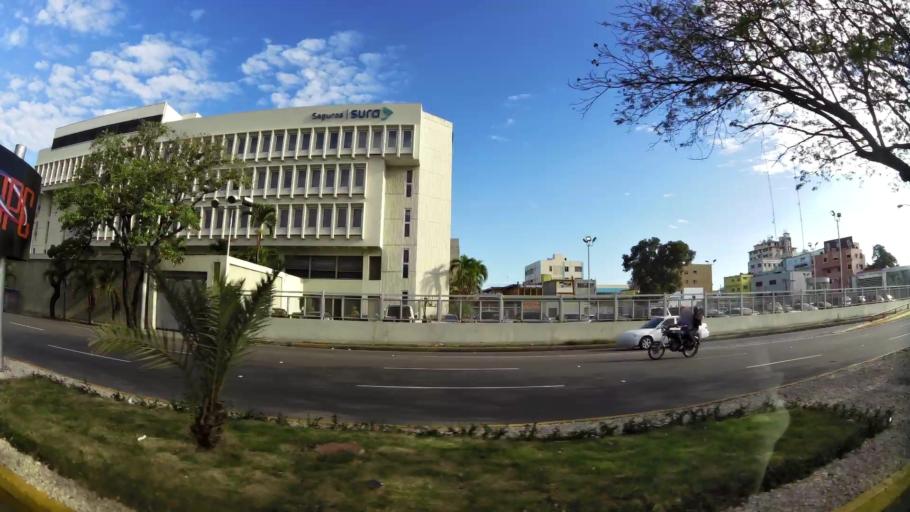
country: DO
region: Nacional
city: San Carlos
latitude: 18.4813
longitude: -69.9075
